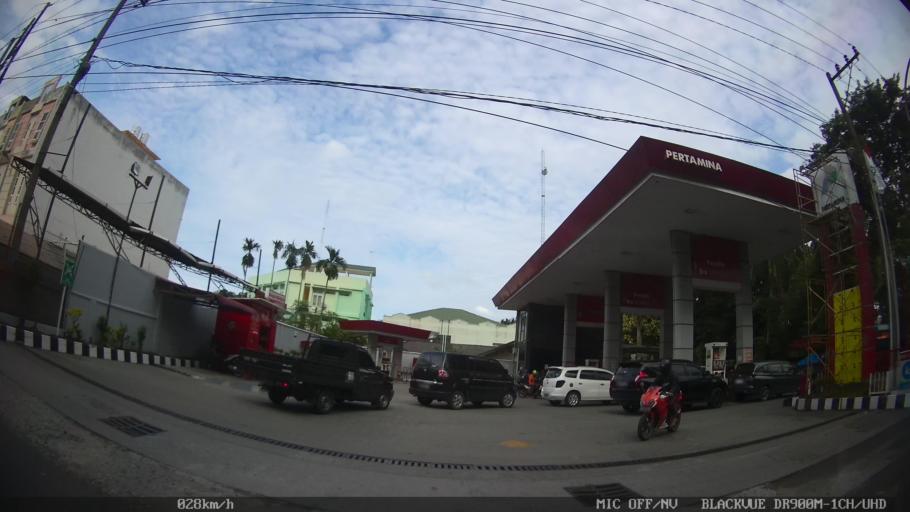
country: ID
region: North Sumatra
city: Medan
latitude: 3.6039
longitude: 98.6797
